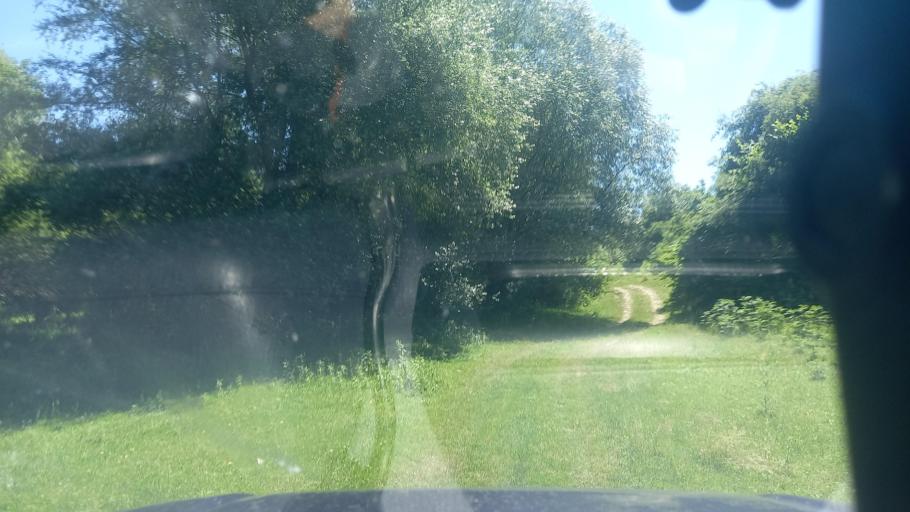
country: RU
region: Karachayevo-Cherkesiya
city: Kurdzhinovo
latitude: 44.1229
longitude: 41.0633
